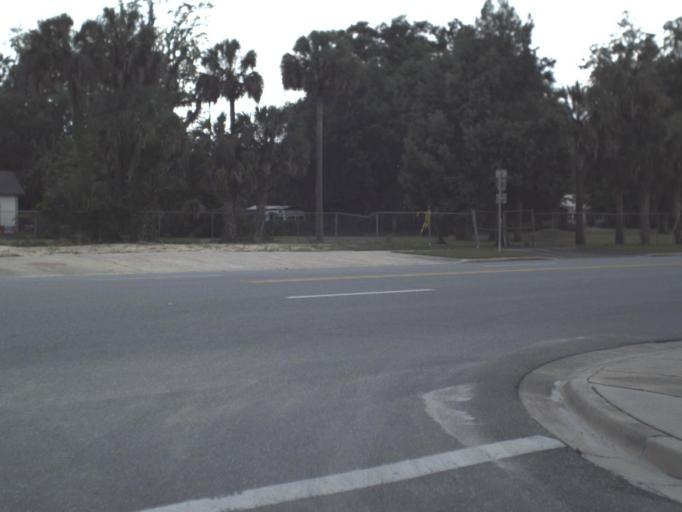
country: US
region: Georgia
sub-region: Echols County
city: Statenville
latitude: 30.6029
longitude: -83.0996
